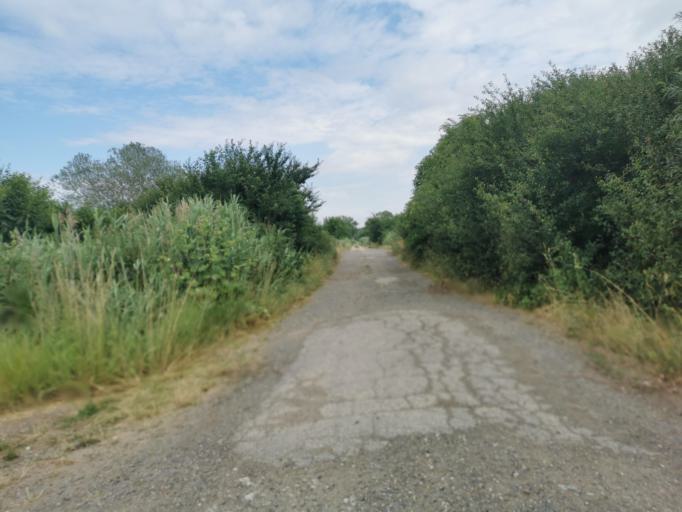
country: CZ
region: South Moravian
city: Tynec
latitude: 48.7645
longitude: 17.0592
